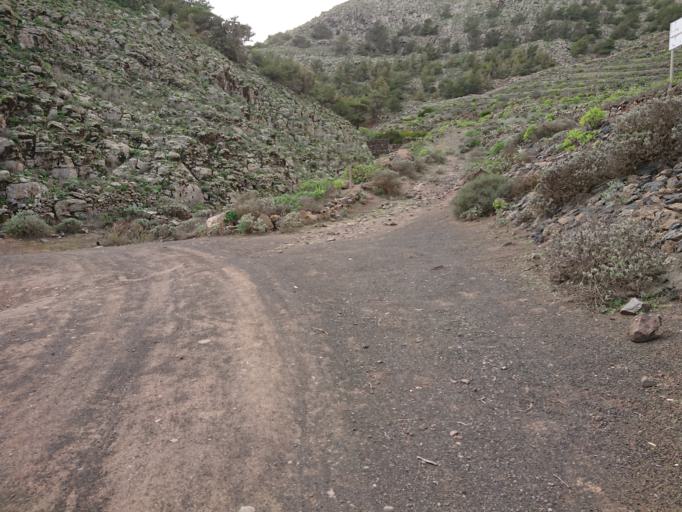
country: ES
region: Canary Islands
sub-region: Provincia de Las Palmas
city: Haria
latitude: 29.1328
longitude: -13.5184
